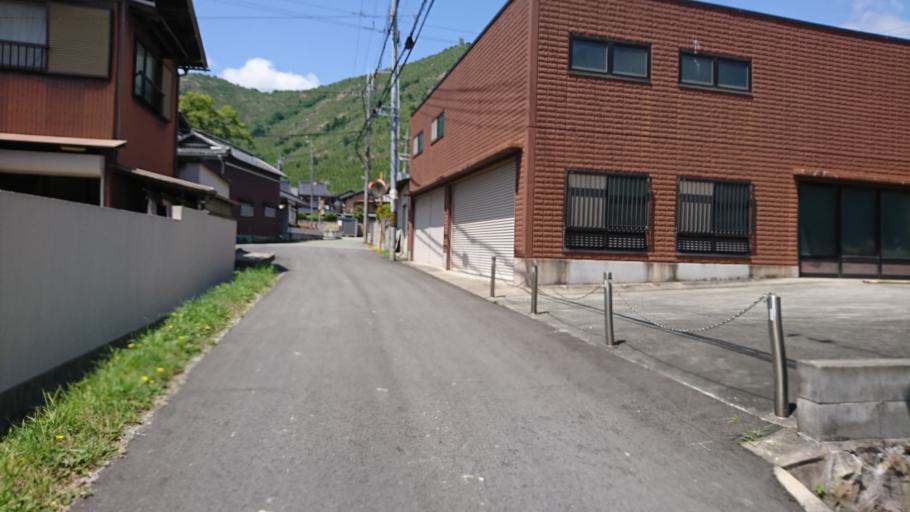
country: JP
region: Hyogo
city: Kakogawacho-honmachi
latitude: 34.8061
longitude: 134.7889
